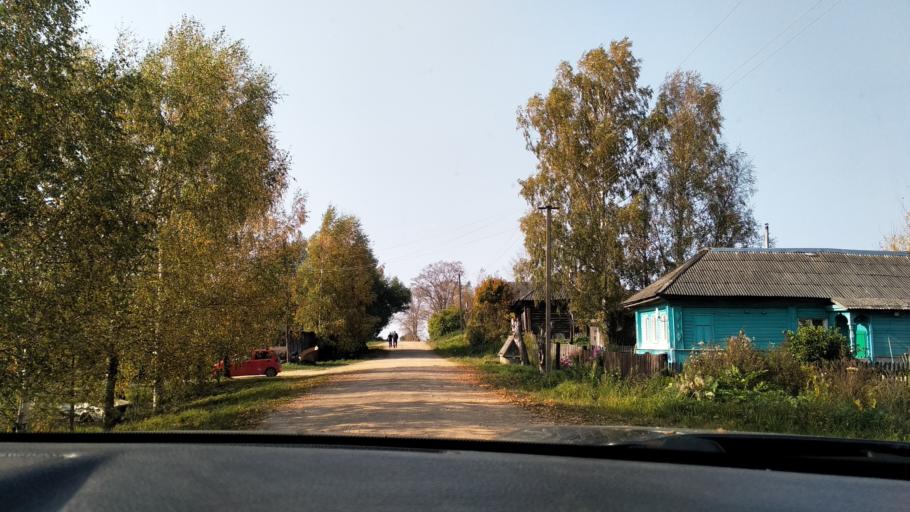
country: RU
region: Tverskaya
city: Krasnyy Kholm
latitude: 58.0337
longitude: 37.1765
